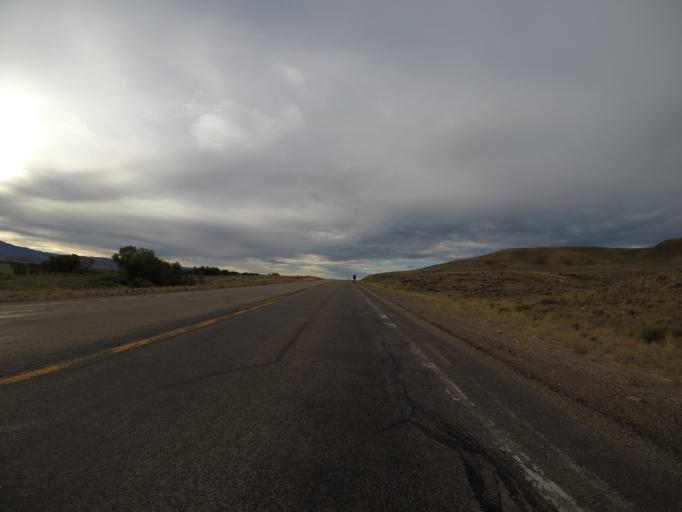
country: US
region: Wyoming
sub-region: Carbon County
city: Saratoga
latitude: 41.4079
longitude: -106.7779
